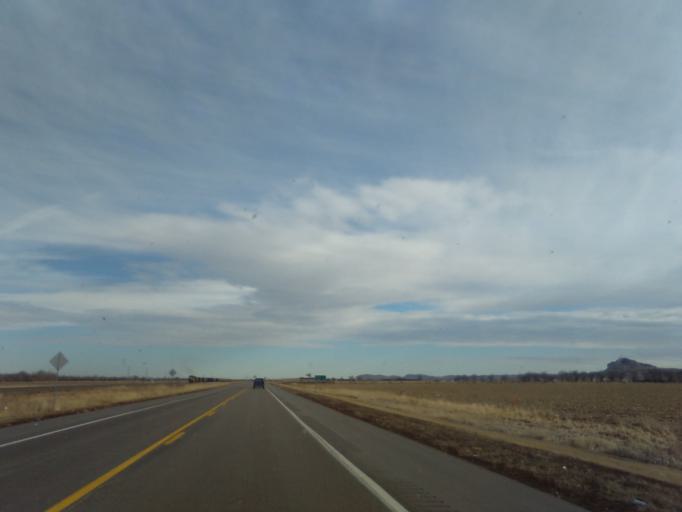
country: US
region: Nebraska
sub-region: Scotts Bluff County
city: Gering
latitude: 41.7821
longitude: -103.5128
